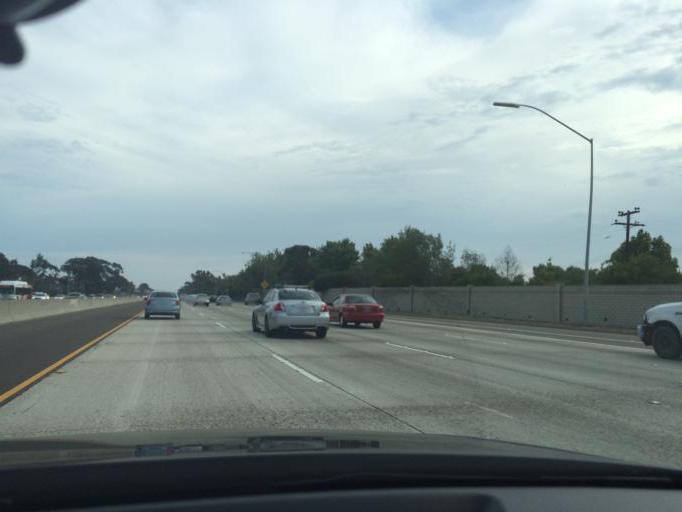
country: US
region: California
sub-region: San Diego County
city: San Diego
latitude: 32.7978
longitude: -117.1569
